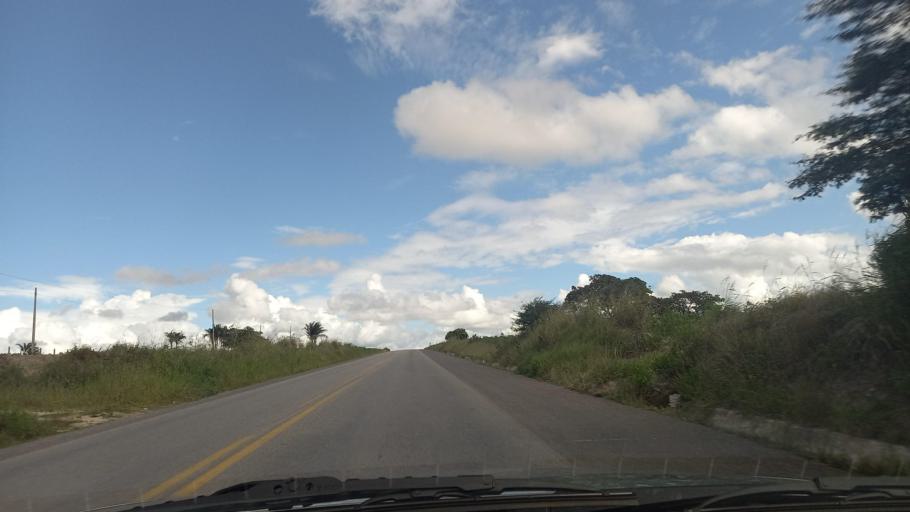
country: BR
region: Pernambuco
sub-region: Lajedo
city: Lajedo
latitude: -8.7324
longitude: -36.4314
